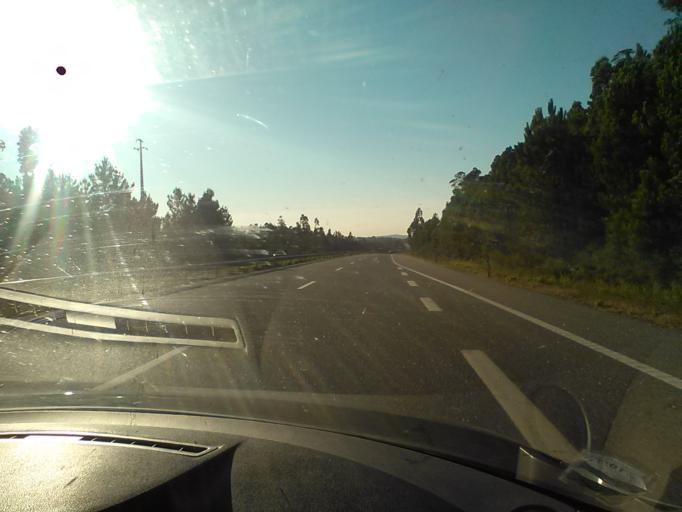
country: PT
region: Braga
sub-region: Vila Nova de Famalicao
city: Ribeirao
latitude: 41.3818
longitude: -8.5761
